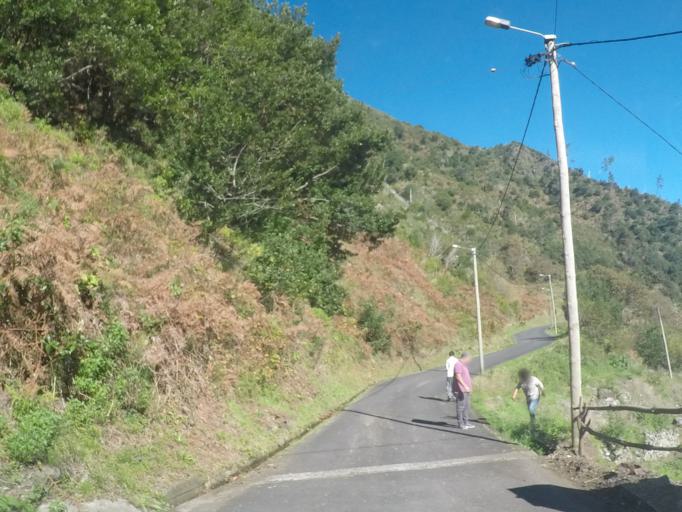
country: PT
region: Madeira
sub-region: Camara de Lobos
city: Curral das Freiras
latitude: 32.7825
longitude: -16.9786
